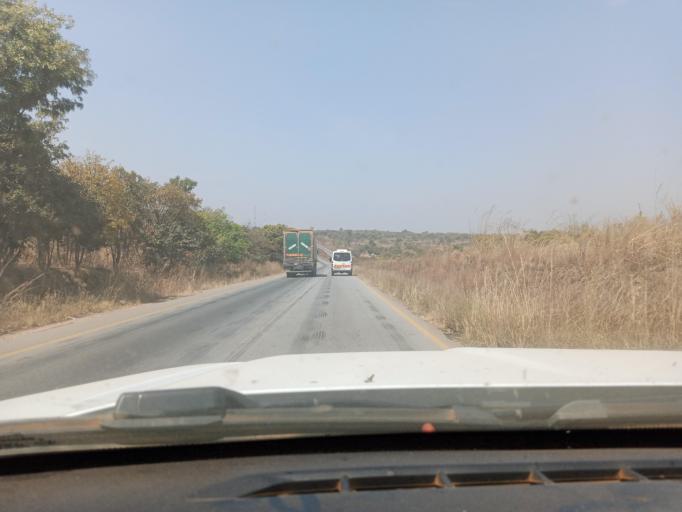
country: ZM
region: Copperbelt
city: Luanshya
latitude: -13.0142
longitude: 28.4345
